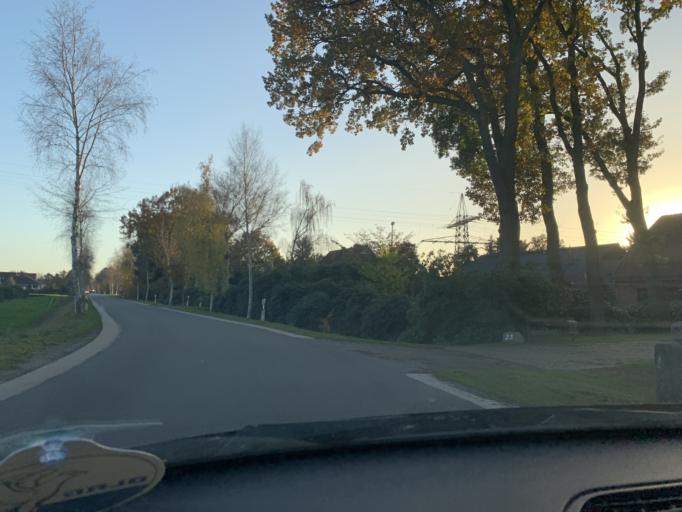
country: DE
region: Lower Saxony
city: Bad Zwischenahn
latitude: 53.1554
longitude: 8.0518
